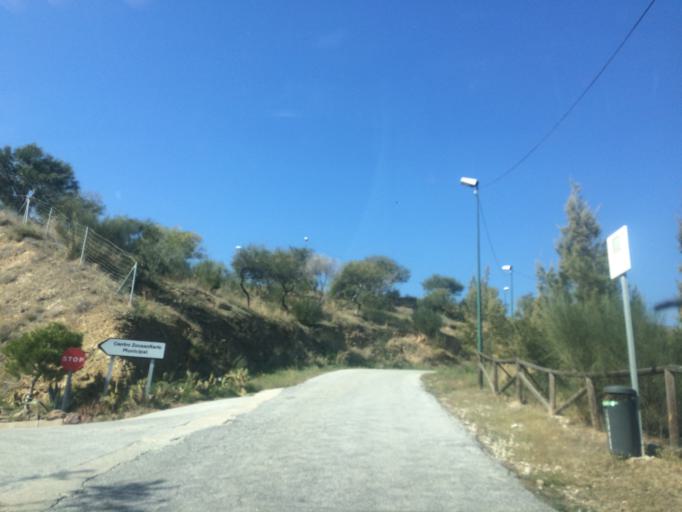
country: ES
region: Andalusia
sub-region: Provincia de Malaga
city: Malaga
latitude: 36.7524
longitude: -4.4359
